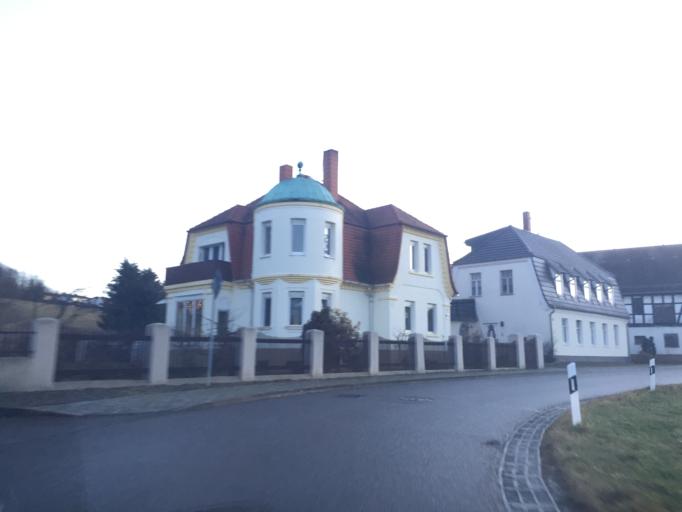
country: DE
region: Thuringia
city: Schmolln
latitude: 50.8797
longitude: 12.3329
